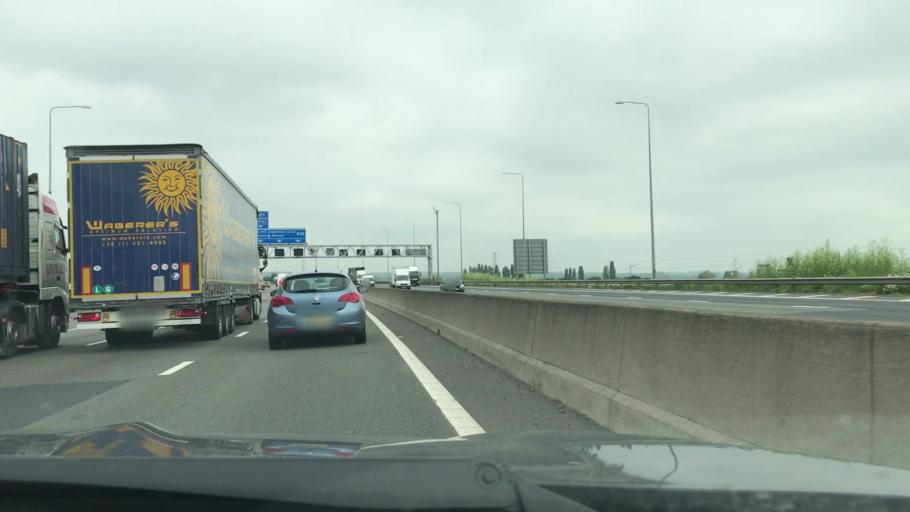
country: GB
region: England
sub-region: Greater London
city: Cranham
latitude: 51.5557
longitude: 0.2892
